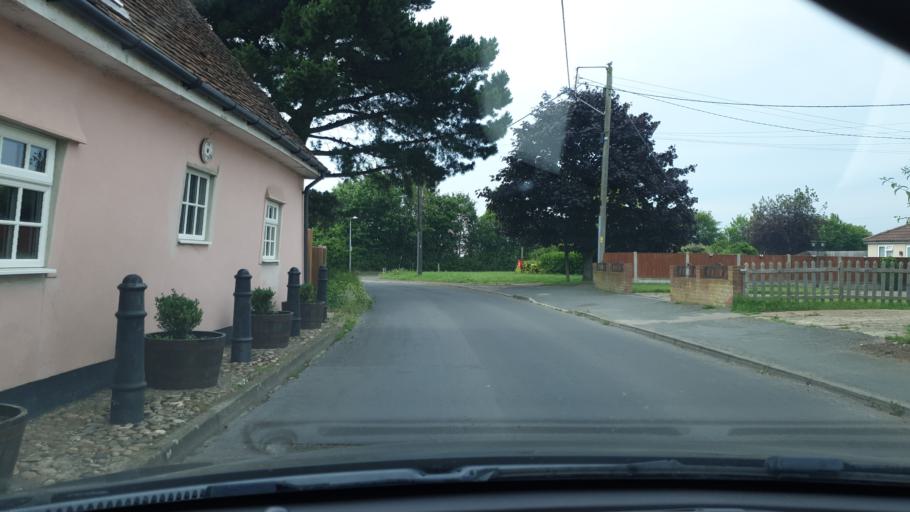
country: GB
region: England
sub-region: Essex
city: Dovercourt
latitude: 51.9178
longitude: 1.2224
